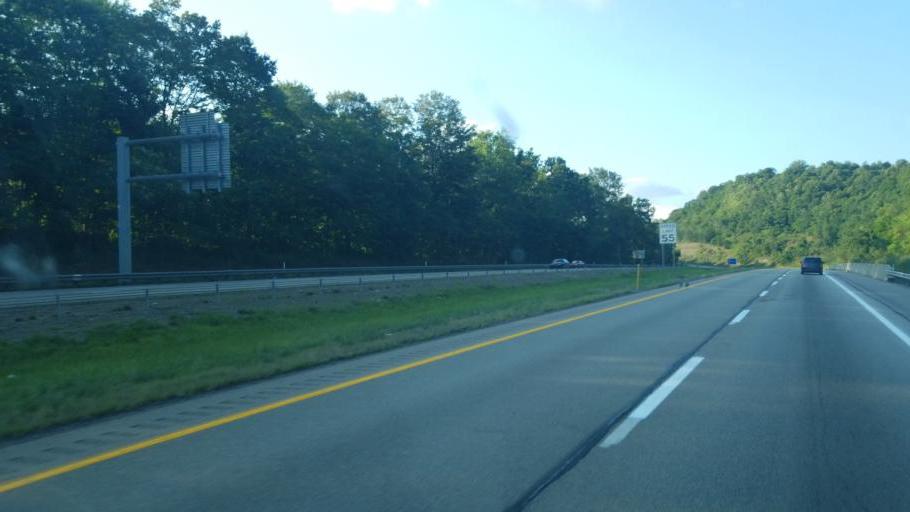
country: US
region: Pennsylvania
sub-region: Allegheny County
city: Emsworth
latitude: 40.5382
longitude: -80.1232
